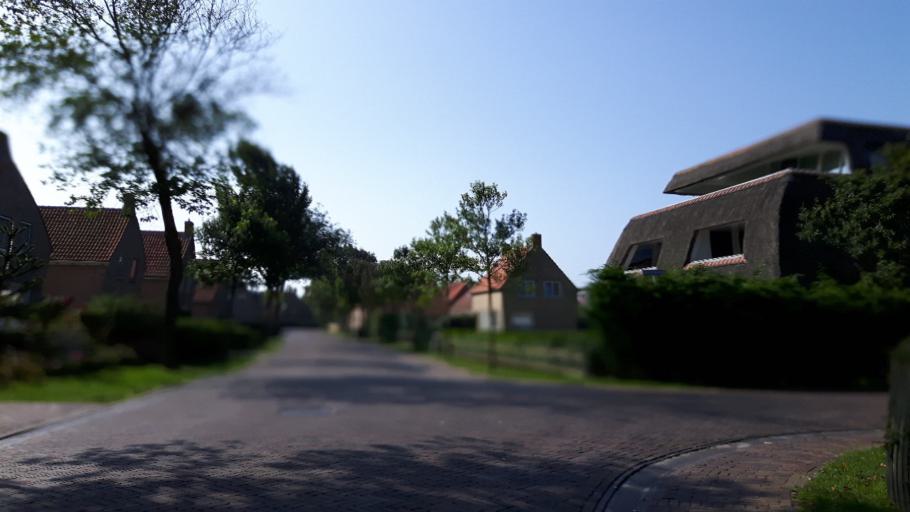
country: NL
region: Friesland
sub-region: Gemeente Ameland
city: Nes
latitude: 53.4490
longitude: 5.8000
